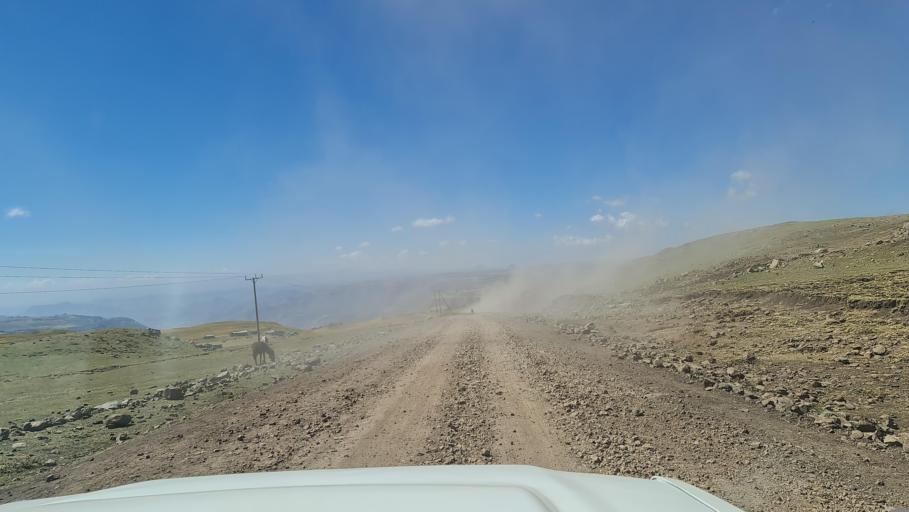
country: ET
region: Amhara
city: Debark'
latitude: 13.2379
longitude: 38.1138
